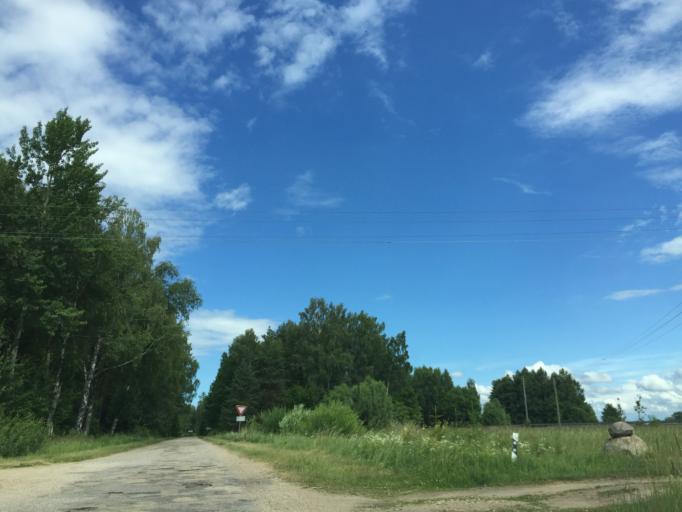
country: LV
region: Saulkrastu
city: Saulkrasti
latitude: 57.4172
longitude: 24.4274
